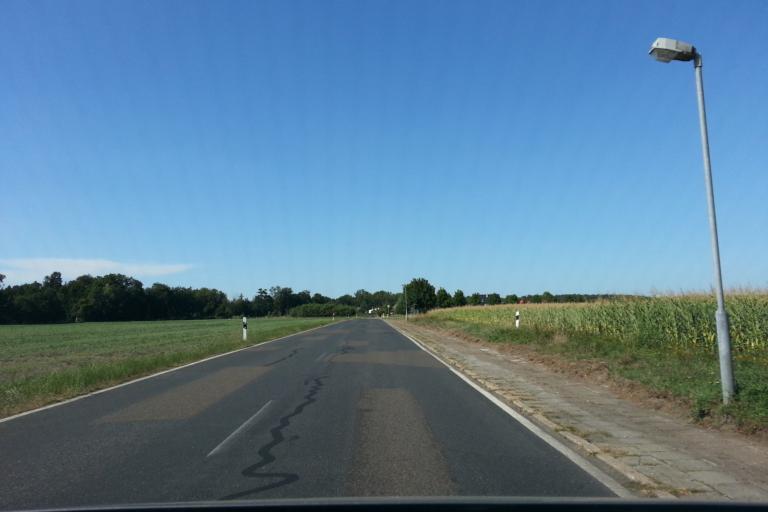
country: DE
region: Mecklenburg-Vorpommern
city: Eggesin
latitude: 53.6762
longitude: 14.0351
